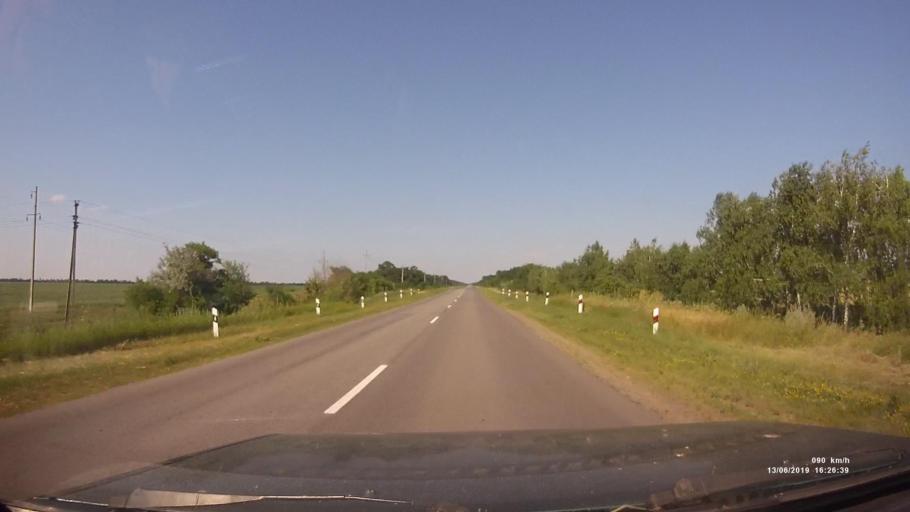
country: RU
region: Rostov
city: Kazanskaya
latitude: 49.8067
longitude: 41.1693
